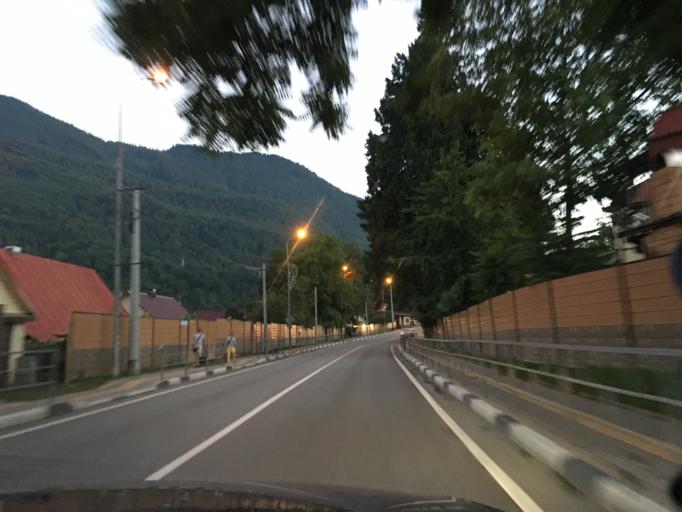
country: RU
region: Krasnodarskiy
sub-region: Sochi City
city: Krasnaya Polyana
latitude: 43.6806
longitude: 40.2122
